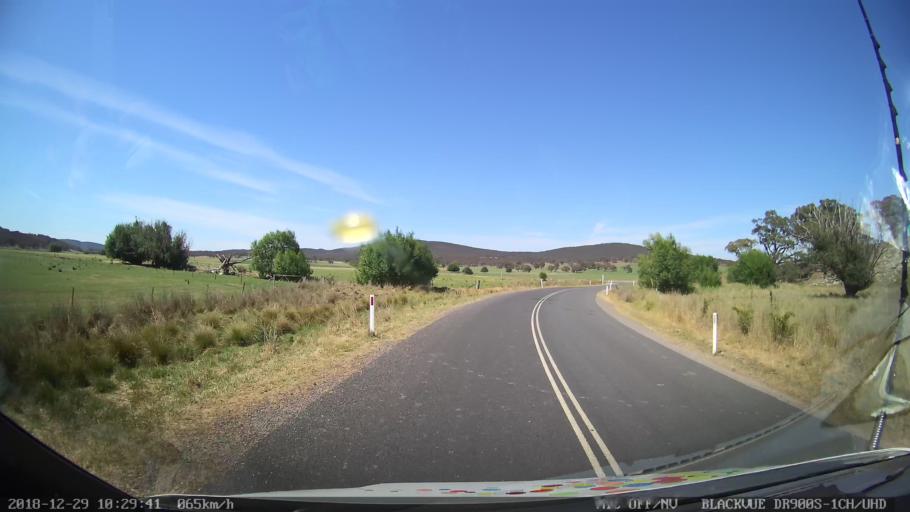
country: AU
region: New South Wales
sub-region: Yass Valley
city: Gundaroo
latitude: -34.9545
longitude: 149.4568
